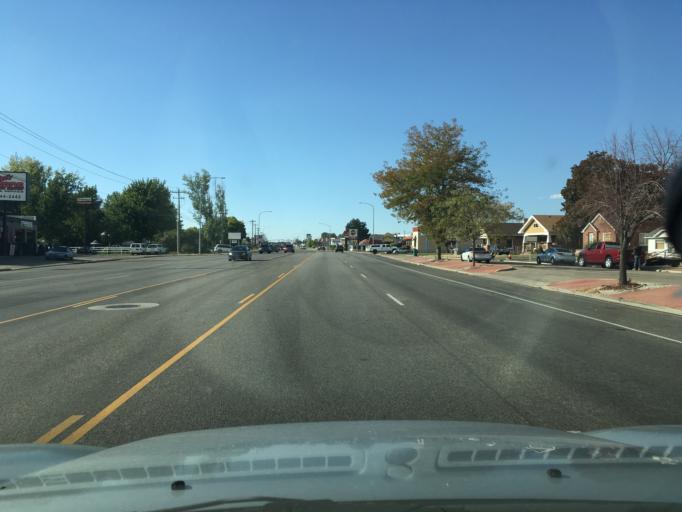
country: US
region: Utah
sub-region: Davis County
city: Layton
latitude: 41.0635
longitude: -111.9692
